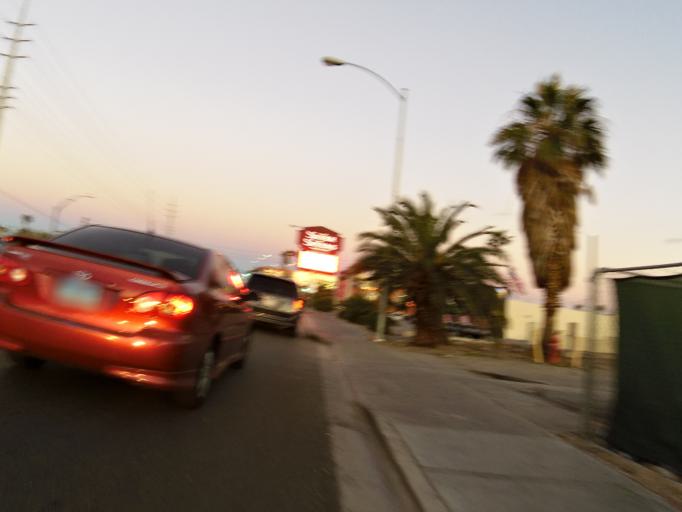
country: US
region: Nevada
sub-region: Clark County
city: Paradise
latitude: 36.1142
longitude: -115.1551
